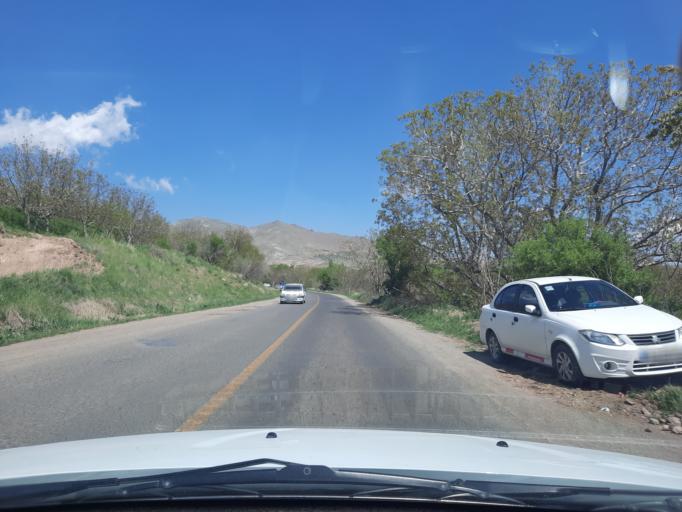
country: IR
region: Qazvin
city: Qazvin
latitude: 36.3428
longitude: 50.1739
